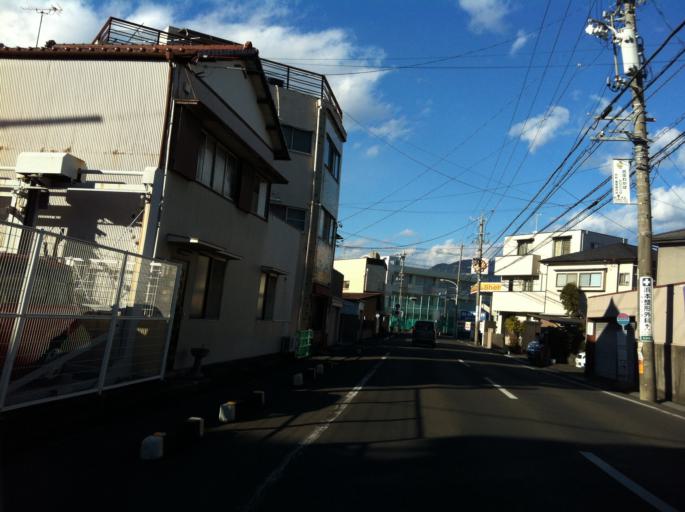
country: JP
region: Shizuoka
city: Shizuoka-shi
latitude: 34.9942
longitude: 138.3862
